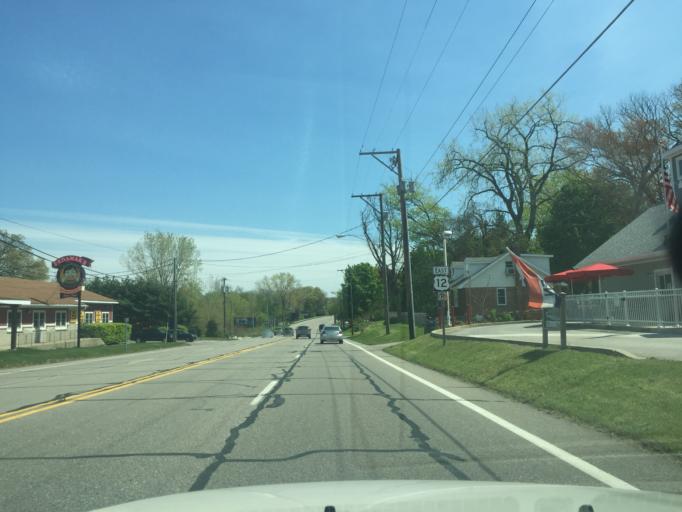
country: US
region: Michigan
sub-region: Berrien County
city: New Buffalo
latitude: 41.7968
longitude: -86.7373
